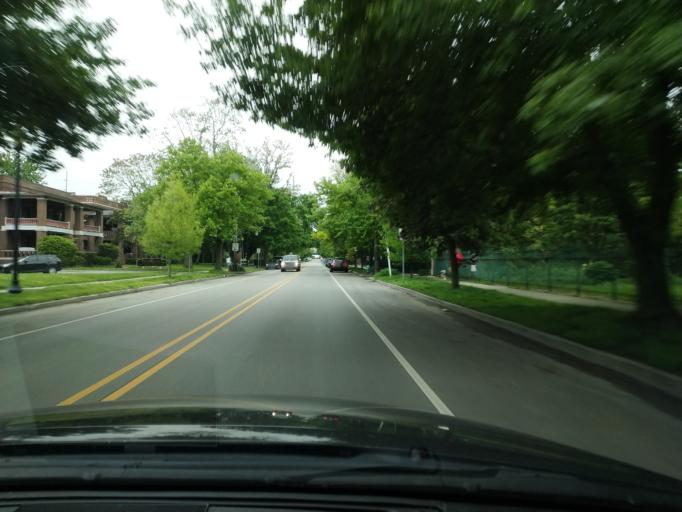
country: US
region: Indiana
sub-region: Marion County
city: Indianapolis
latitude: 39.7859
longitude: -86.1495
